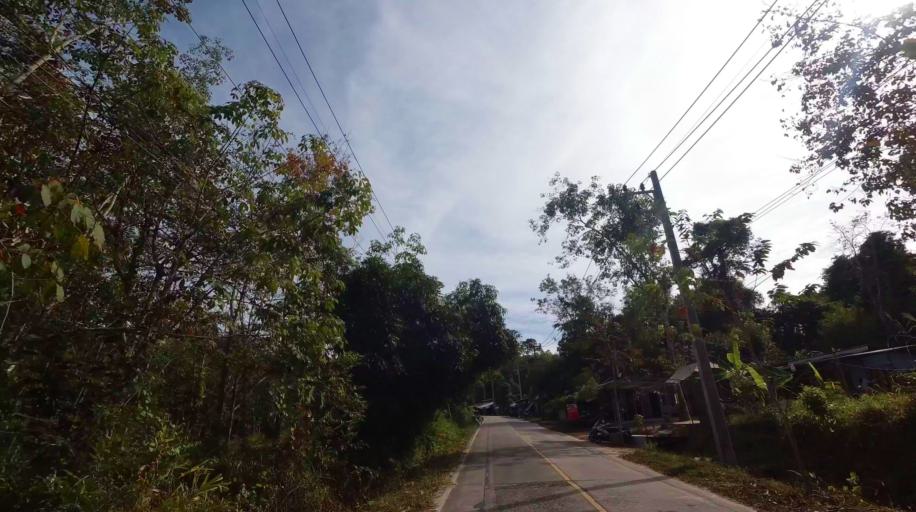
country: TH
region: Trat
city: Ko Kut
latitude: 11.6100
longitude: 102.5418
